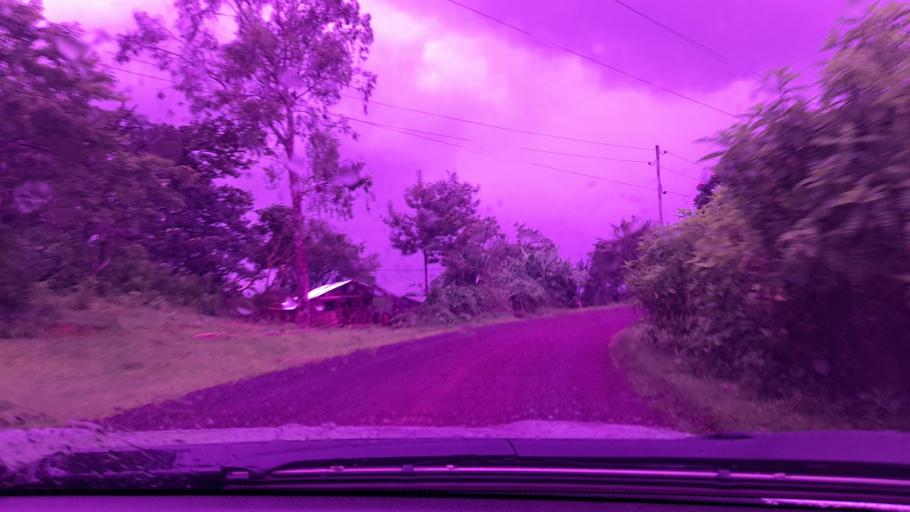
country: ET
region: Oromiya
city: Metu
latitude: 8.4419
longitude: 35.6206
